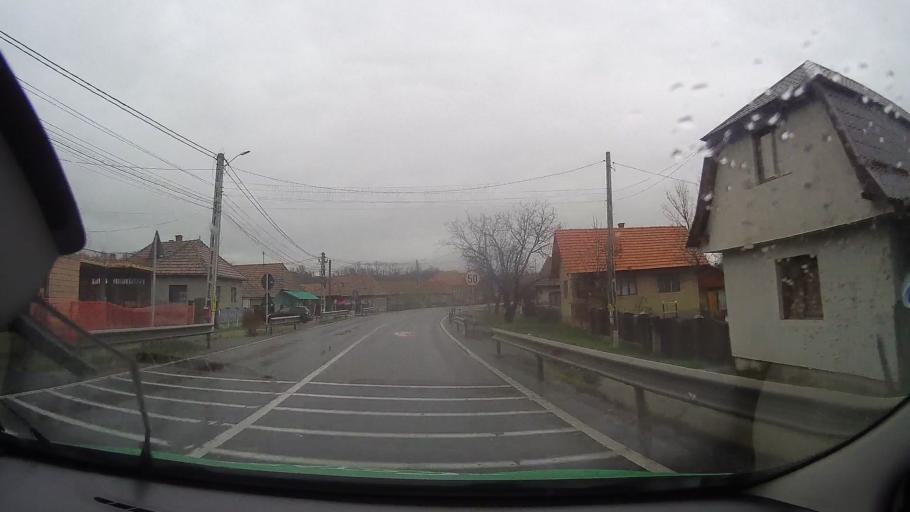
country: RO
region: Mures
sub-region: Comuna Brancovenesti
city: Brancovenesti
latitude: 46.8549
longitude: 24.7567
